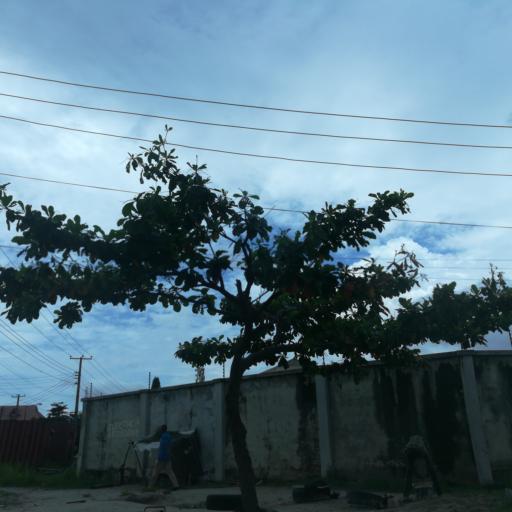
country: NG
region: Lagos
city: Ikoyi
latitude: 6.4427
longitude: 3.4690
